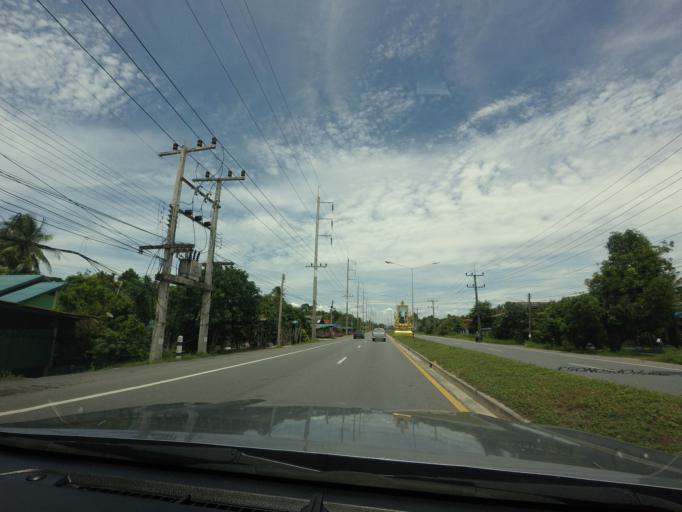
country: TH
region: Songkhla
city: Krasae Sin
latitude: 7.5956
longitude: 100.4033
